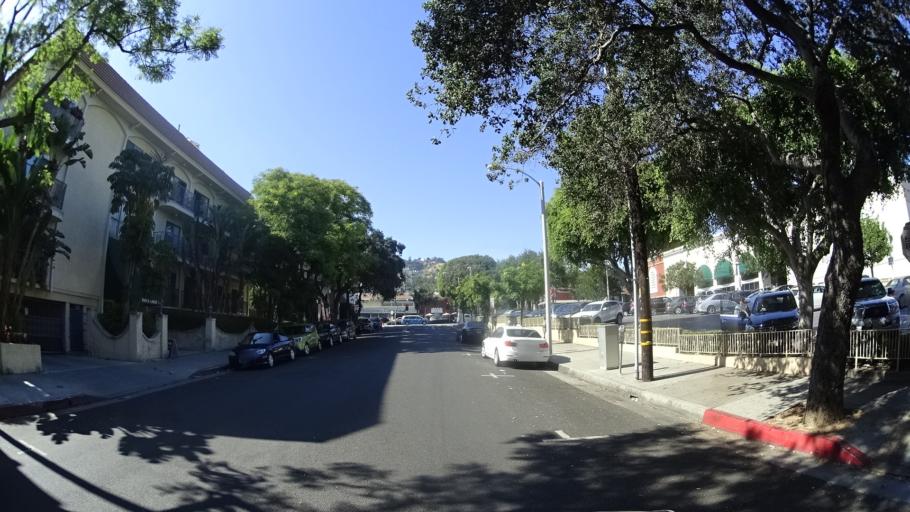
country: US
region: California
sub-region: Los Angeles County
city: West Hollywood
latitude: 34.0900
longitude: -118.3717
